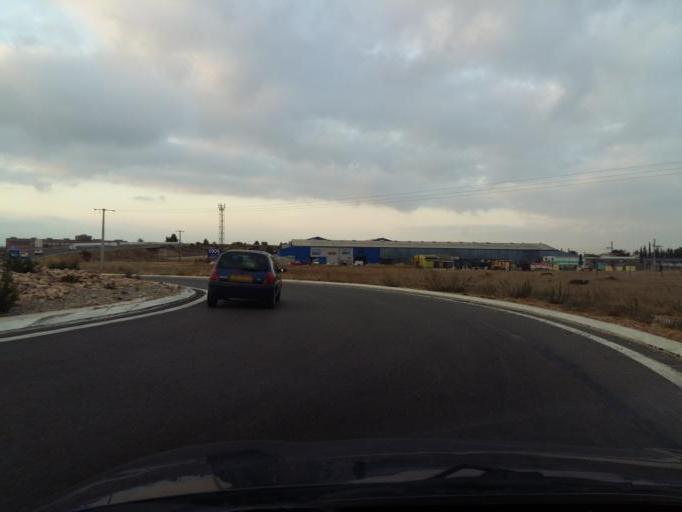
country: FR
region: Provence-Alpes-Cote d'Azur
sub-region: Departement des Bouches-du-Rhone
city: Miramas
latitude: 43.5885
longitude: 4.9893
